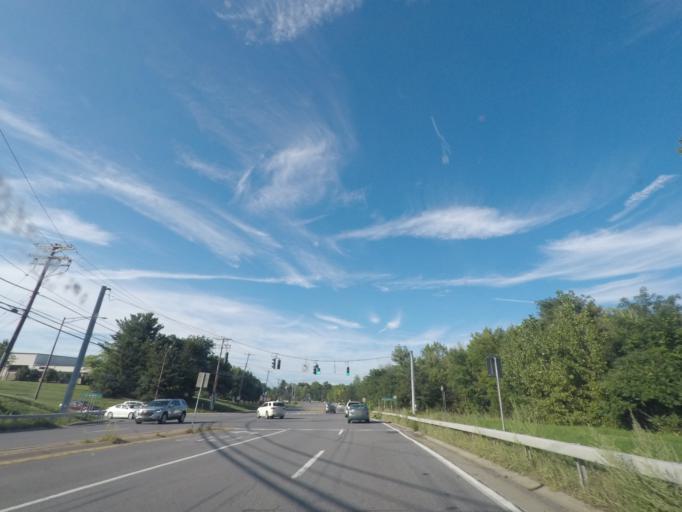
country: US
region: New York
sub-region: Schenectady County
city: Niskayuna
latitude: 42.7581
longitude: -73.8147
